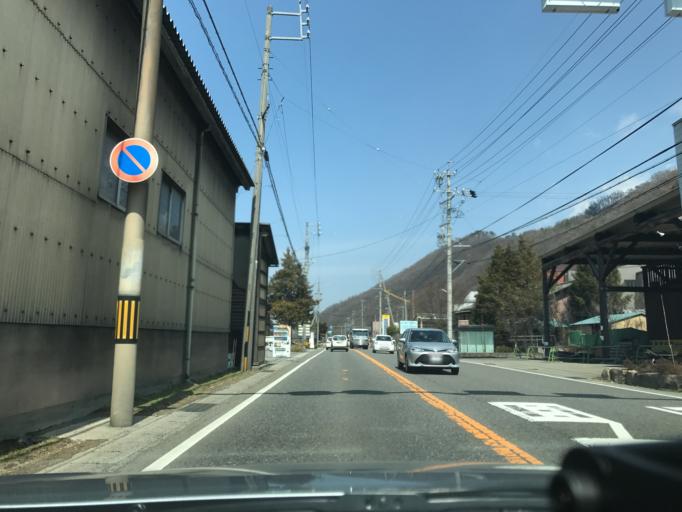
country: JP
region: Nagano
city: Matsumoto
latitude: 36.2494
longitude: 137.9518
